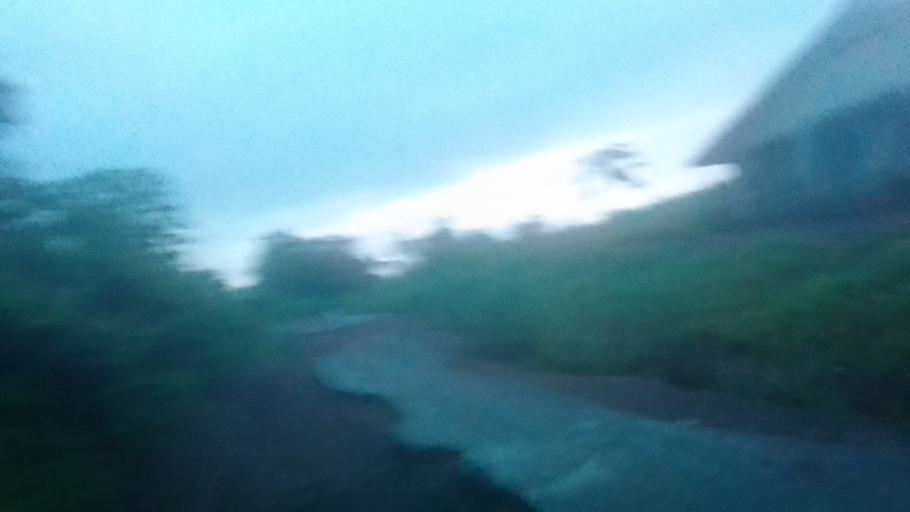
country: SL
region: Northern Province
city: Lunsar
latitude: 8.7066
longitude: -12.5217
